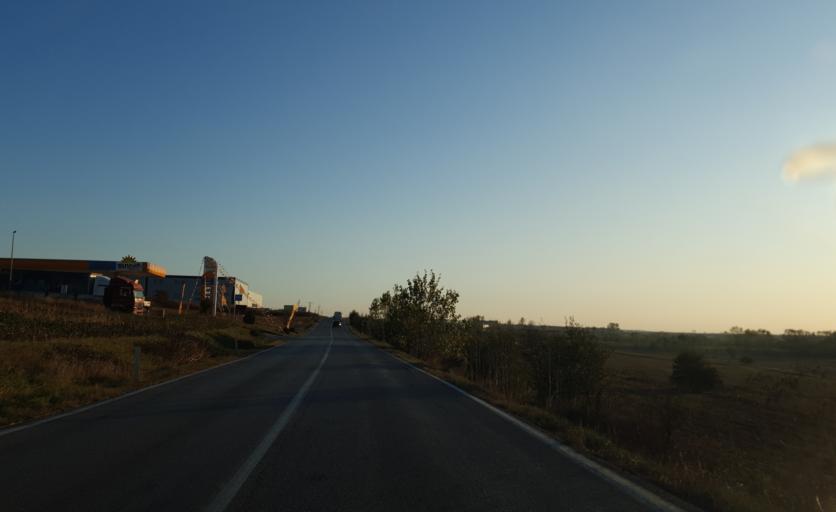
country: TR
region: Tekirdag
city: Beyazkoy
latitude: 41.3447
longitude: 27.7132
